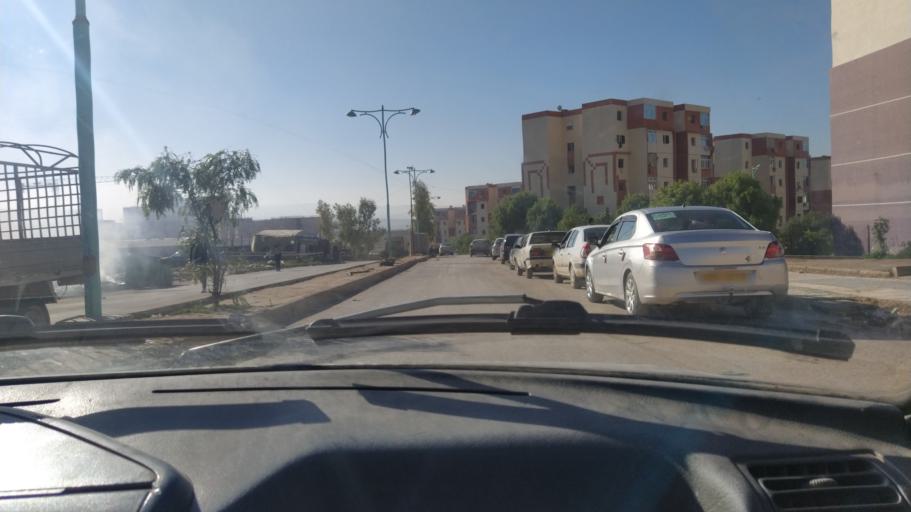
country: DZ
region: Constantine
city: Ain Smara
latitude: 36.2511
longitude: 6.5574
